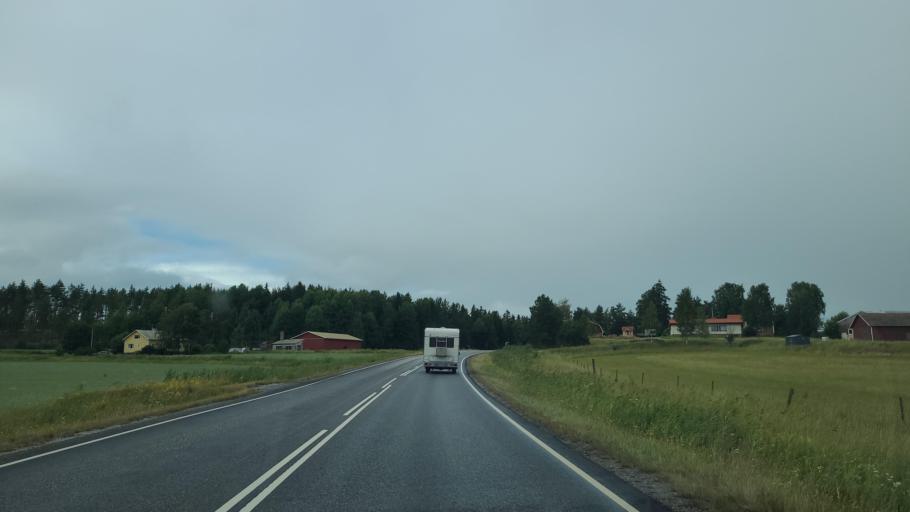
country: FI
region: Varsinais-Suomi
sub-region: Turku
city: Sauvo
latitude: 60.2890
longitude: 22.6729
